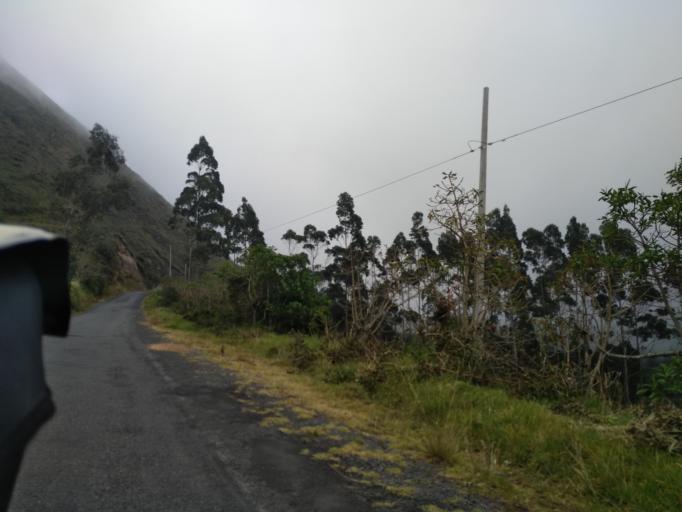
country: EC
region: Cotopaxi
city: Saquisili
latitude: -0.6909
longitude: -78.8261
